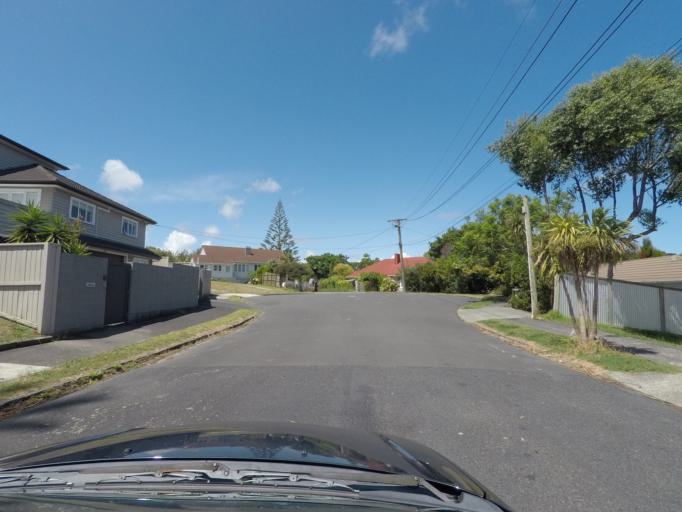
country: NZ
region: Auckland
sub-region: Auckland
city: Auckland
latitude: -36.8584
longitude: 174.7217
